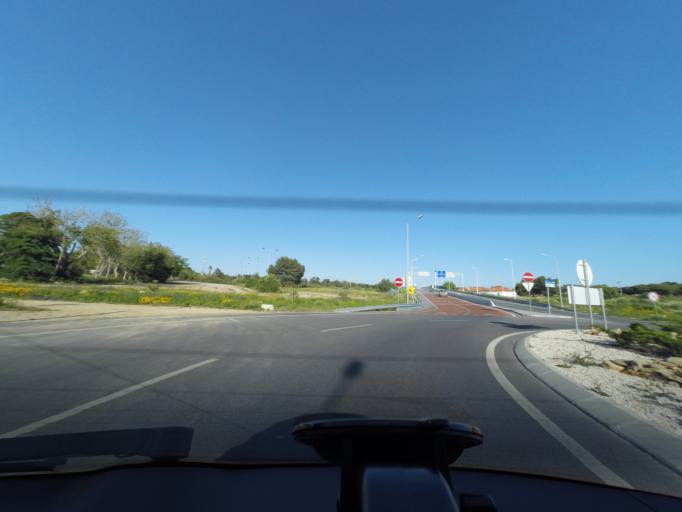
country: PT
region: Lisbon
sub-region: Cascais
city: Cascais
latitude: 38.7224
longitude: -9.4471
